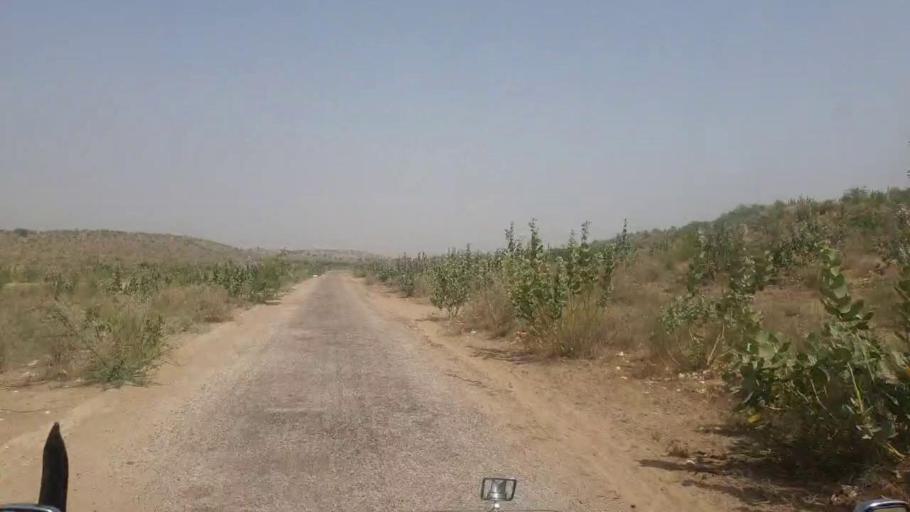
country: PK
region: Sindh
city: Islamkot
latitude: 25.1883
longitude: 70.1987
